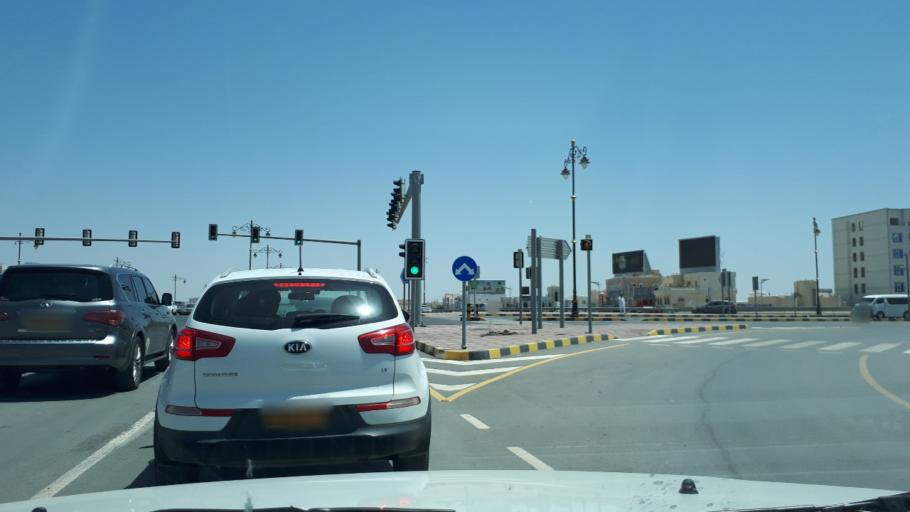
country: OM
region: Muhafazat ad Dakhiliyah
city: Nizwa
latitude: 22.8760
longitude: 57.5333
